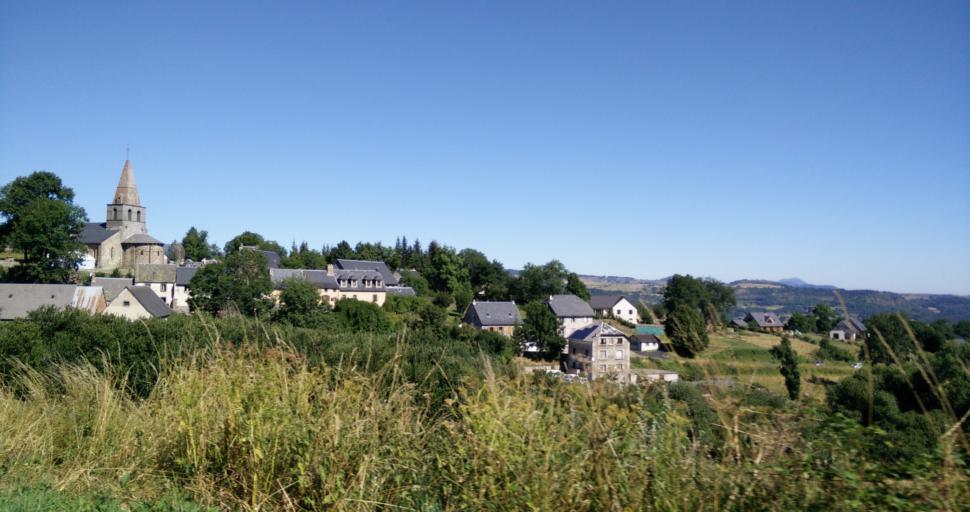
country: FR
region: Auvergne
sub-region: Departement du Puy-de-Dome
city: Aydat
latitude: 45.5499
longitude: 2.9419
